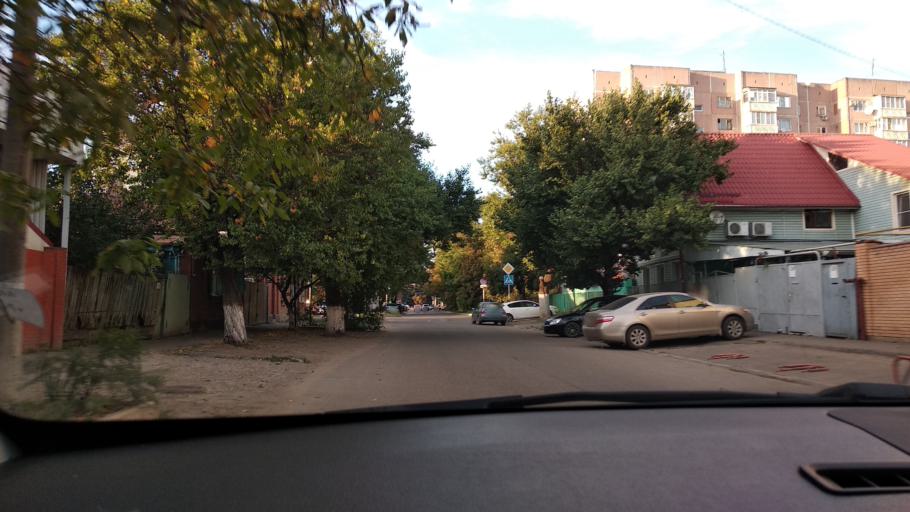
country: RU
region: Krasnodarskiy
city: Krasnodar
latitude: 45.0185
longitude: 39.0044
